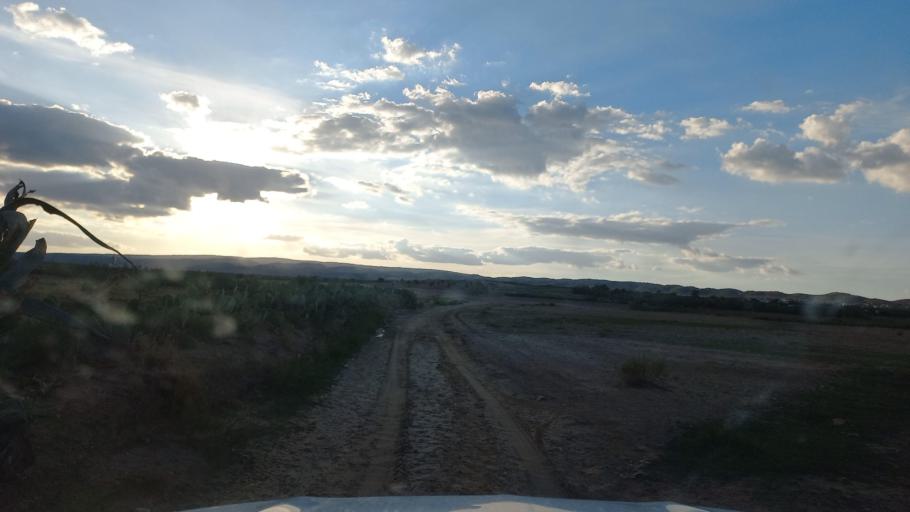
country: TN
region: Al Qasrayn
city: Sbiba
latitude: 35.3529
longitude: 9.0308
